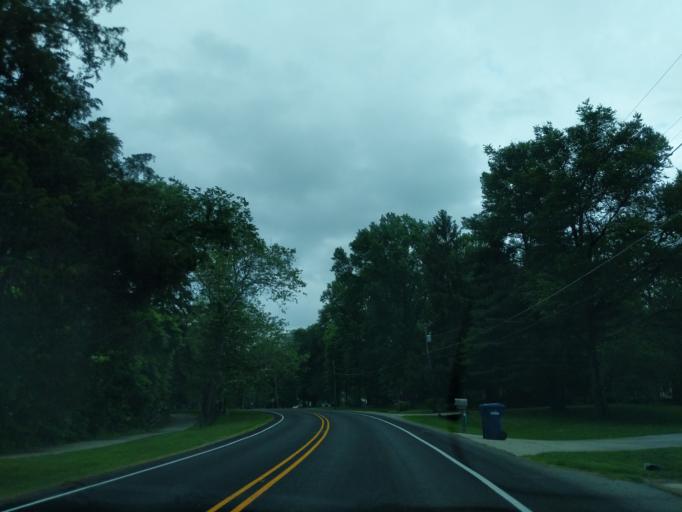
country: US
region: Indiana
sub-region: Madison County
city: Chesterfield
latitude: 40.0941
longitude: -85.6199
